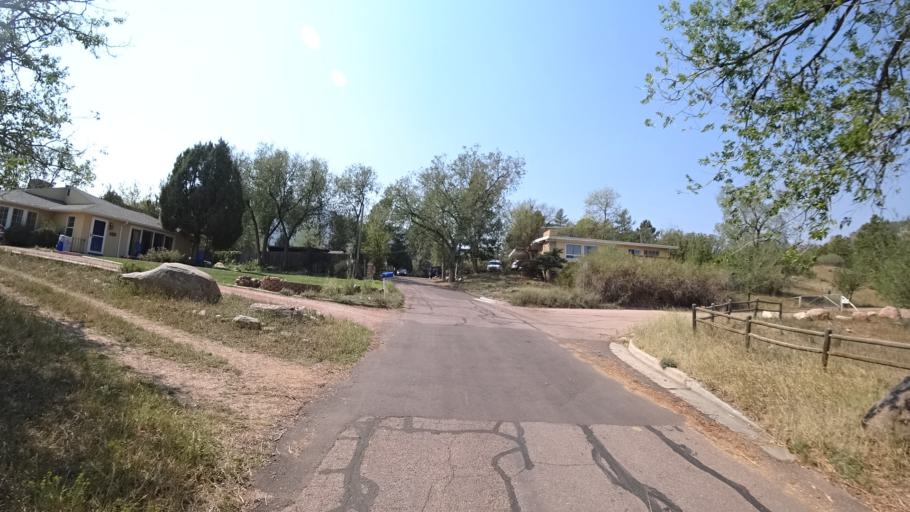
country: US
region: Colorado
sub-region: El Paso County
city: Colorado Springs
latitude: 38.7944
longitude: -104.8591
